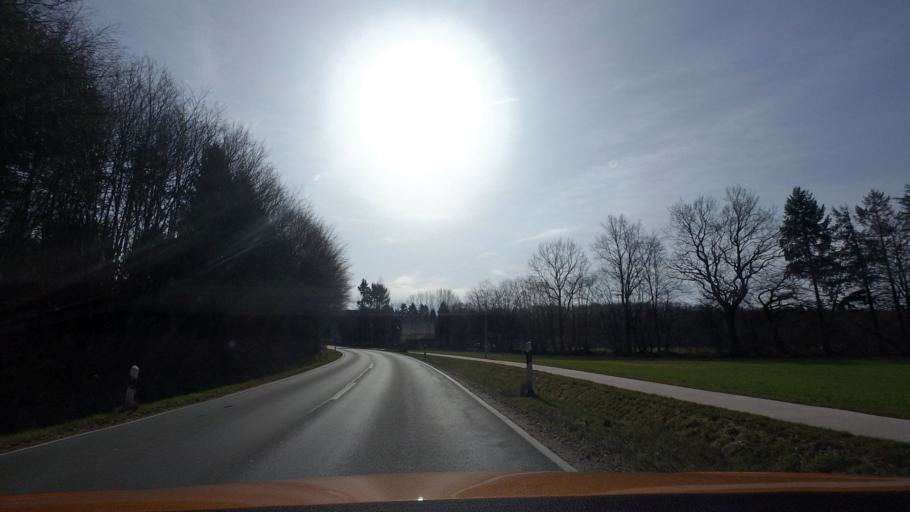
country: DE
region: Lower Saxony
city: Wiedensahl
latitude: 52.3725
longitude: 9.1271
